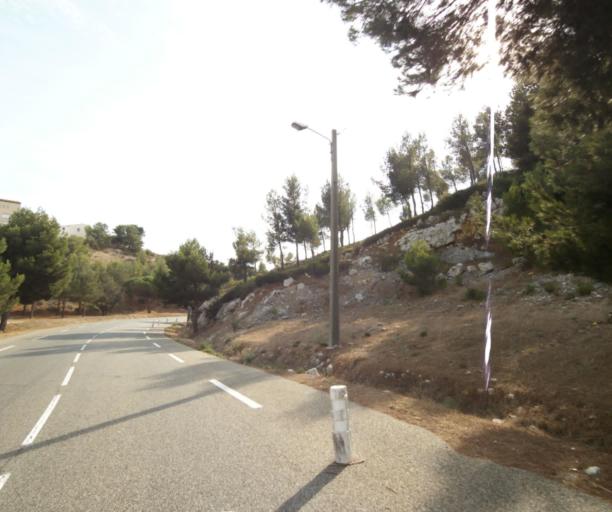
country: FR
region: Provence-Alpes-Cote d'Azur
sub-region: Departement des Bouches-du-Rhone
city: Sausset-les-Pins
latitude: 43.3367
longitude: 5.1087
